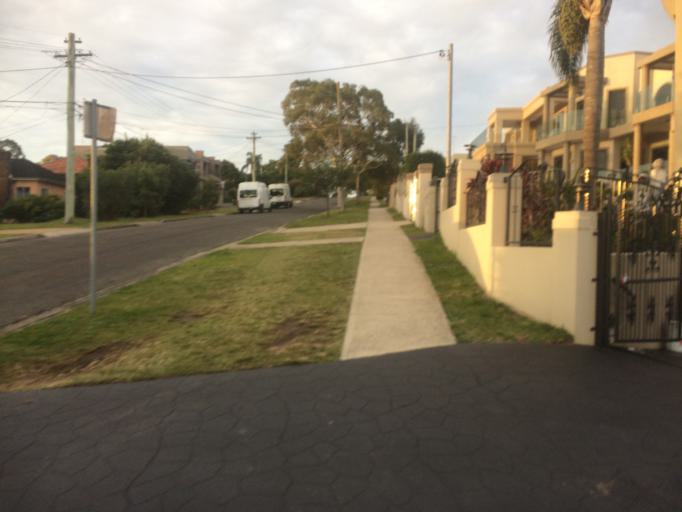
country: AU
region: New South Wales
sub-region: Canada Bay
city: Rhodes
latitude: -33.8298
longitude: 151.1033
